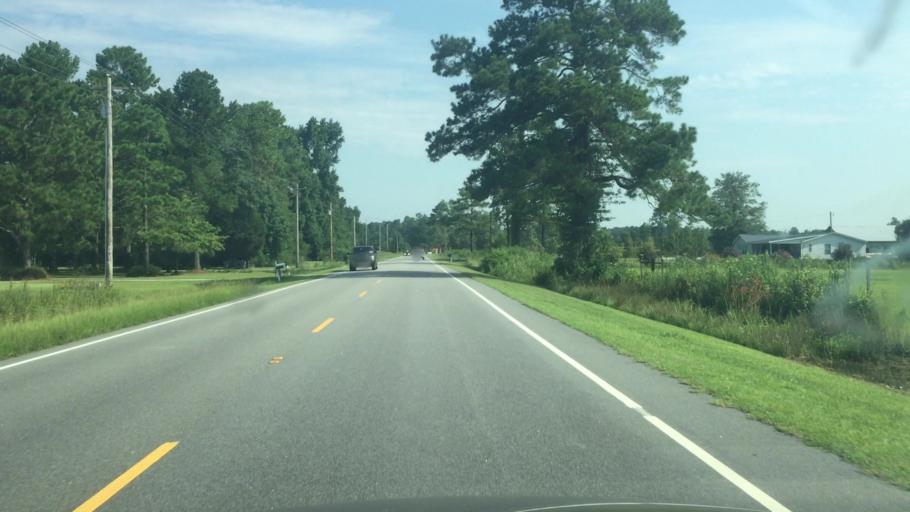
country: US
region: North Carolina
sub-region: Columbus County
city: Chadbourn
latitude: 34.2284
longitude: -78.8243
